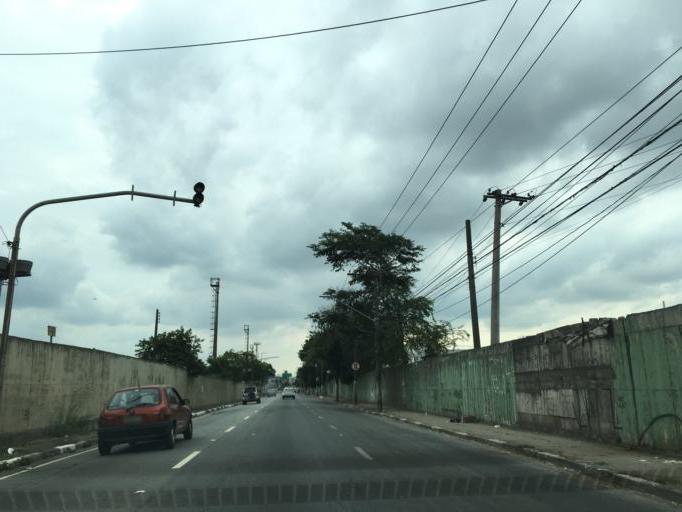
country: BR
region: Sao Paulo
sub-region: Osasco
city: Osasco
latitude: -23.5392
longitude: -46.7396
